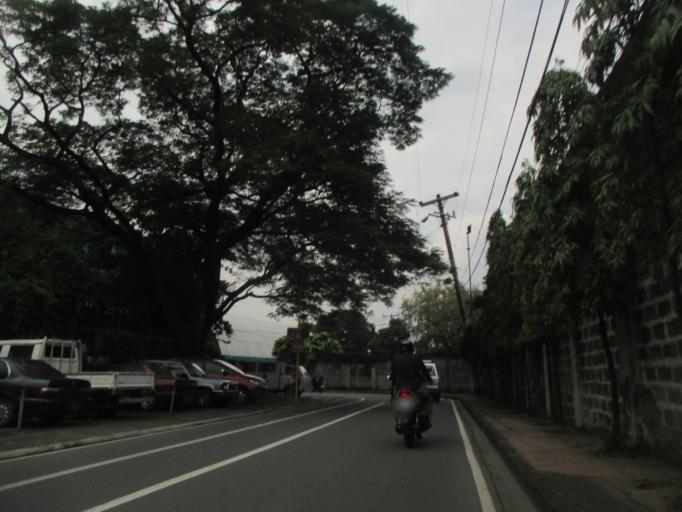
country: PH
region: Metro Manila
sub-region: Marikina
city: Calumpang
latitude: 14.6345
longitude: 121.0856
